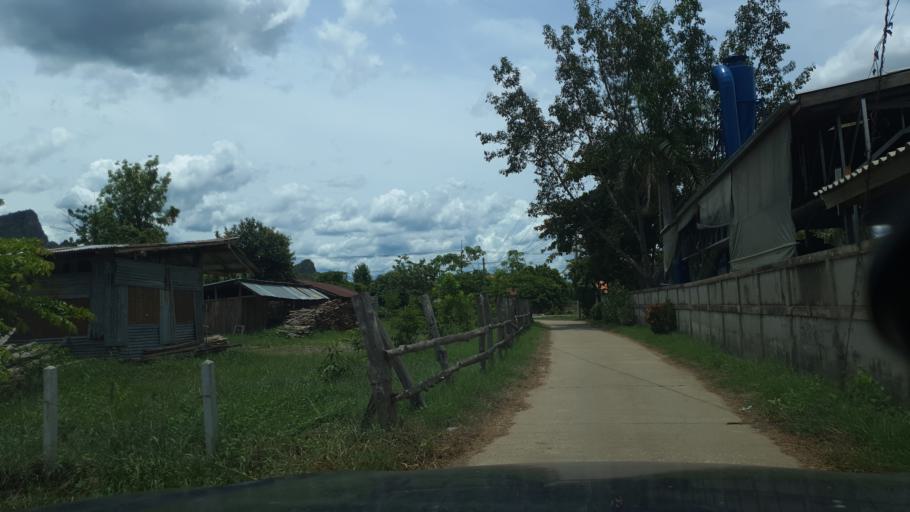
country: TH
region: Sukhothai
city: Thung Saliam
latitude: 17.3284
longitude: 99.5154
